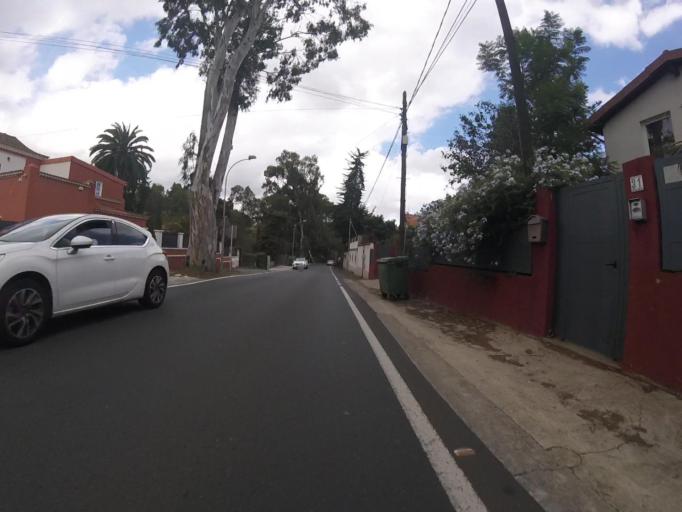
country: ES
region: Canary Islands
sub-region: Provincia de Las Palmas
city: Santa Brigida
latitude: 28.0277
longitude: -15.5023
